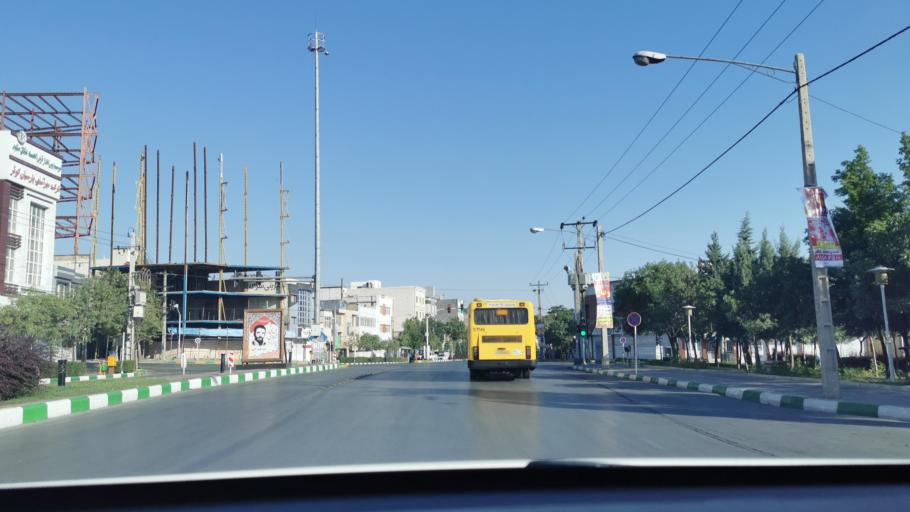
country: IR
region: Razavi Khorasan
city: Mashhad
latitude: 36.3066
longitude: 59.5092
